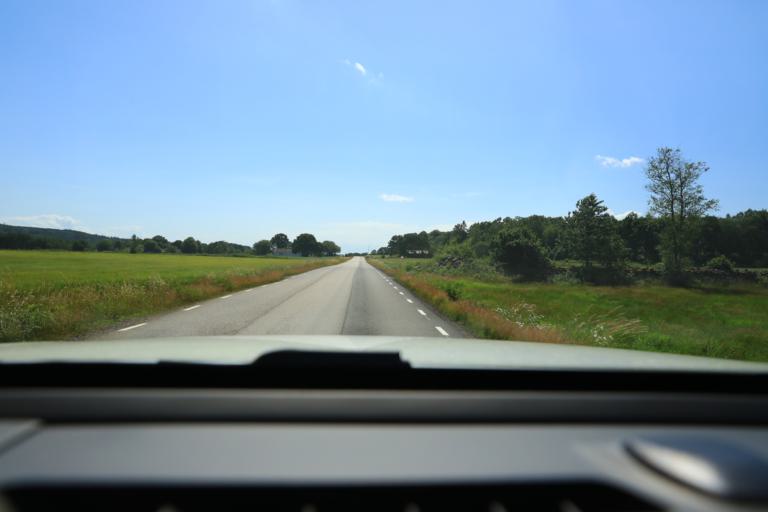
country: SE
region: Halland
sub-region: Varbergs Kommun
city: Tvaaker
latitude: 57.0945
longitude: 12.4079
